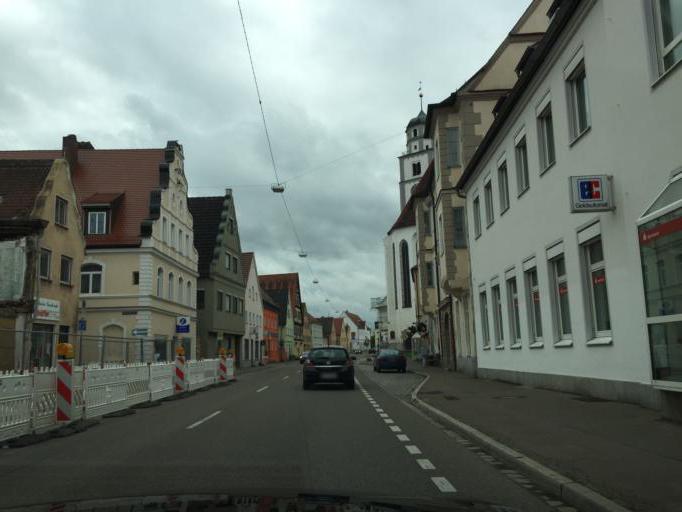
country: DE
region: Bavaria
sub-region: Swabia
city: Lauingen
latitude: 48.5691
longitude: 10.4288
